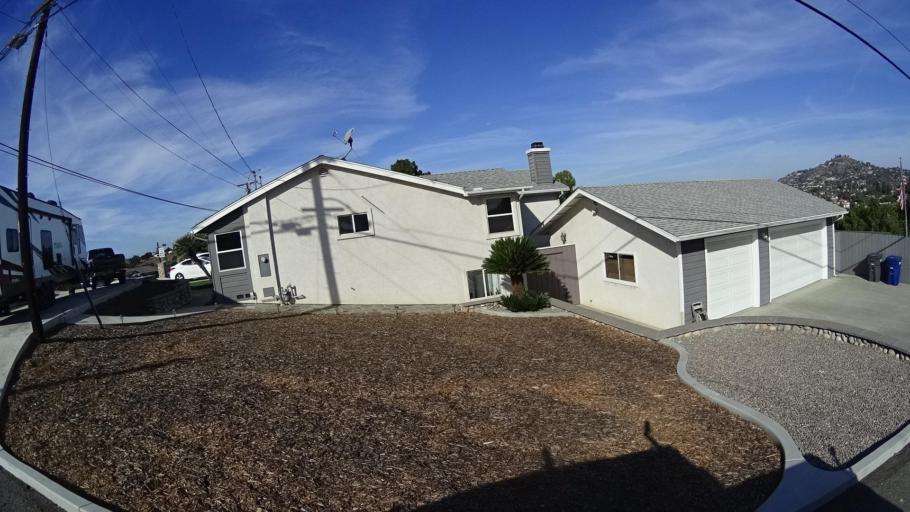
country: US
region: California
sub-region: San Diego County
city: Casa de Oro-Mount Helix
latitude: 32.7400
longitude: -116.9698
